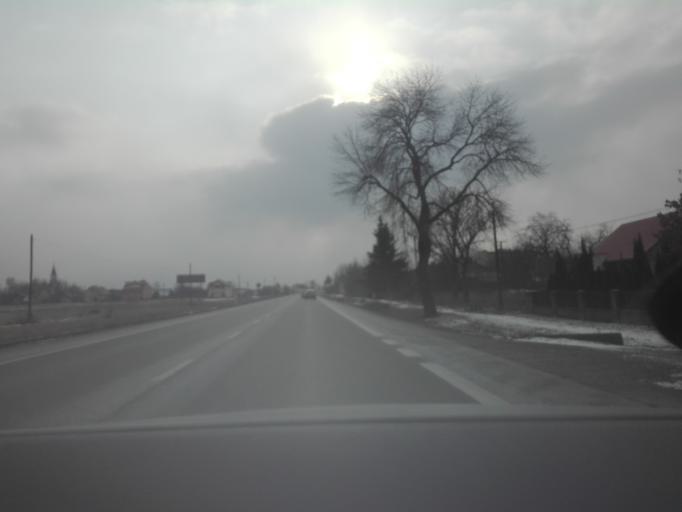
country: PL
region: Subcarpathian Voivodeship
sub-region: Powiat tarnobrzeski
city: Sokolniki
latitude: 50.6606
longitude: 21.7879
